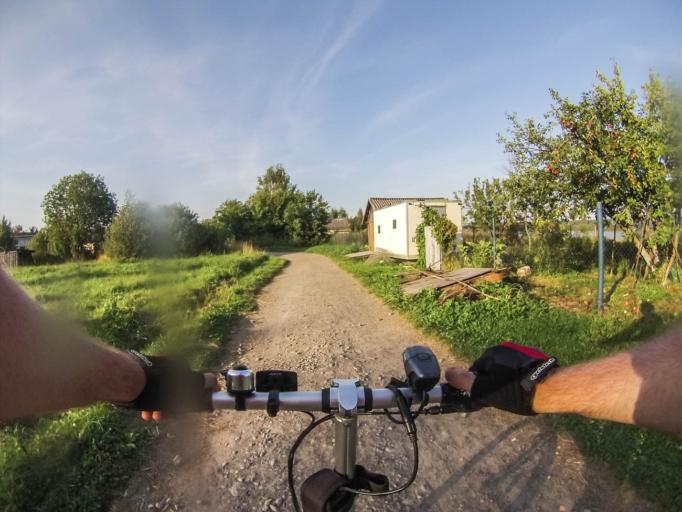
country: RU
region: Jaroslavl
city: Myshkin
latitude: 57.7485
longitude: 38.4383
